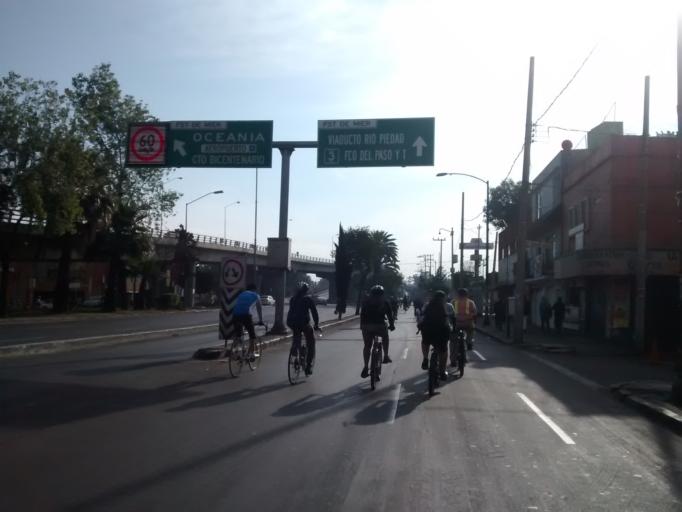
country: MX
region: Mexico City
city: Mexico City
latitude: 19.4207
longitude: -99.1156
